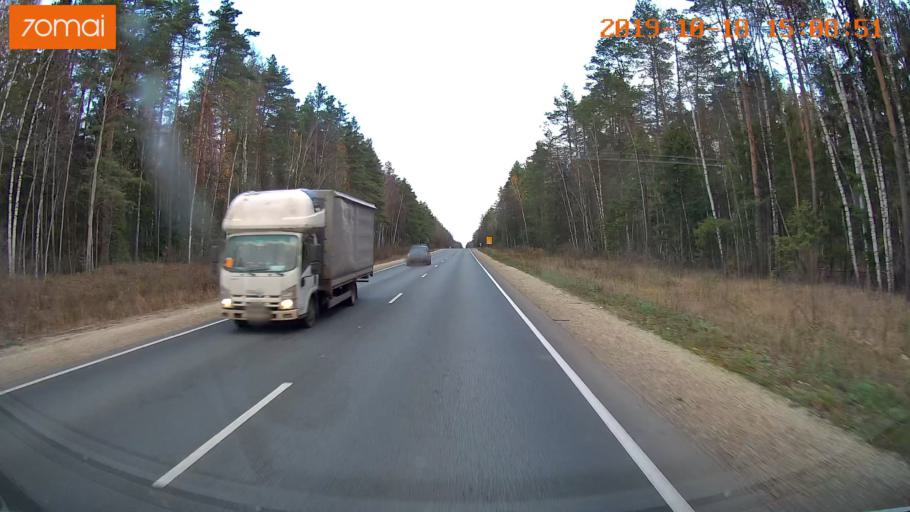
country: RU
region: Vladimir
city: Gus'-Khrustal'nyy
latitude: 55.5580
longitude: 40.6149
